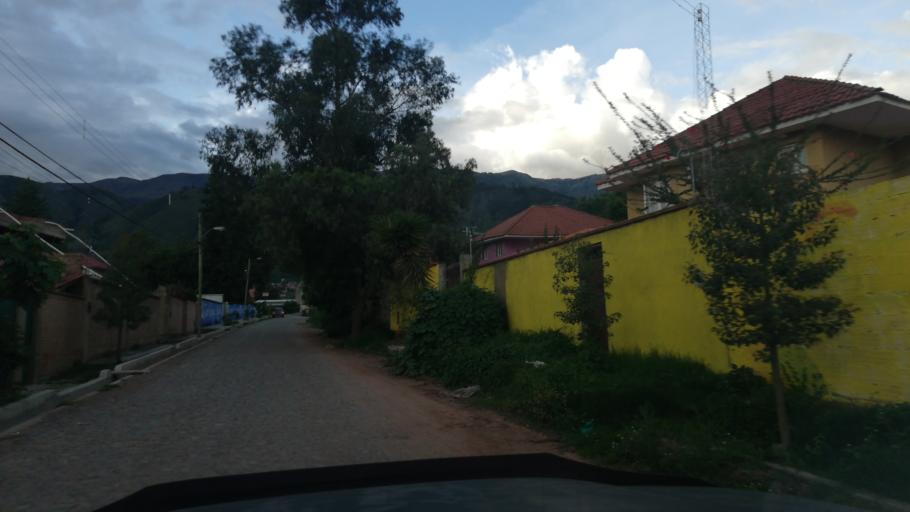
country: BO
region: Cochabamba
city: Cochabamba
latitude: -17.3350
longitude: -66.2221
